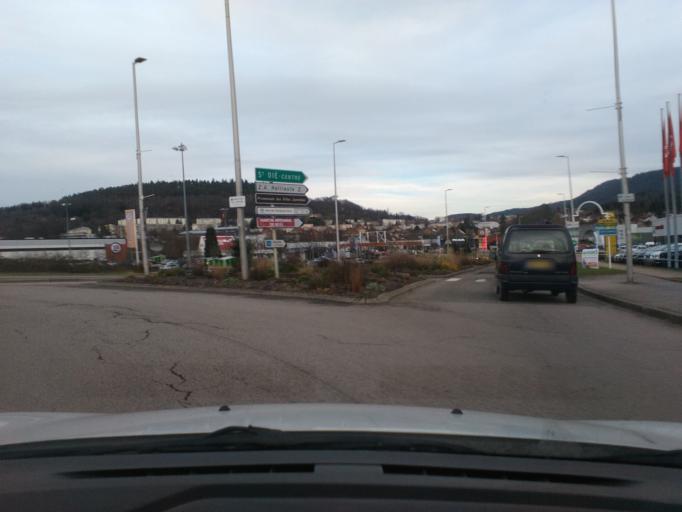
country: FR
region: Lorraine
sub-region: Departement des Vosges
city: Saint-Die-des-Vosges
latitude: 48.2918
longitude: 6.9324
